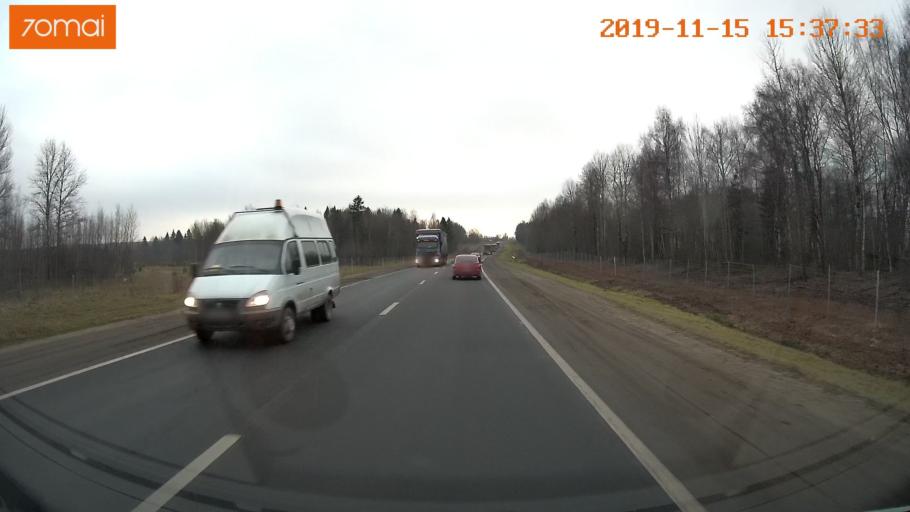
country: RU
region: Jaroslavl
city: Danilov
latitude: 58.0384
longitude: 40.0881
